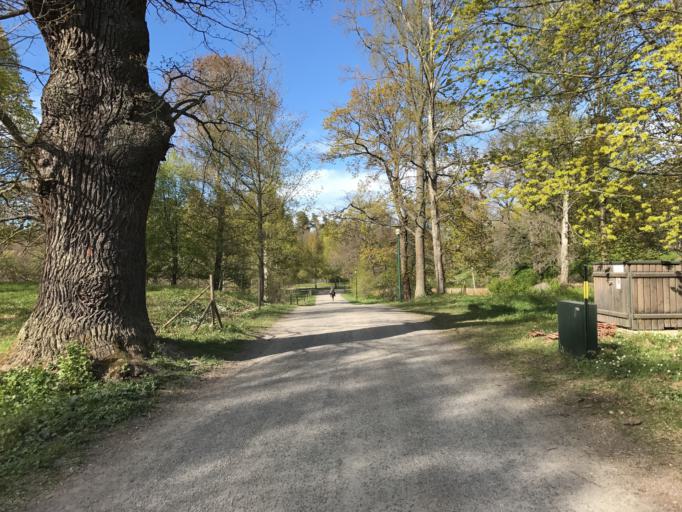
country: SE
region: Stockholm
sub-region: Nacka Kommun
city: Nacka
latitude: 59.3251
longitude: 18.1452
